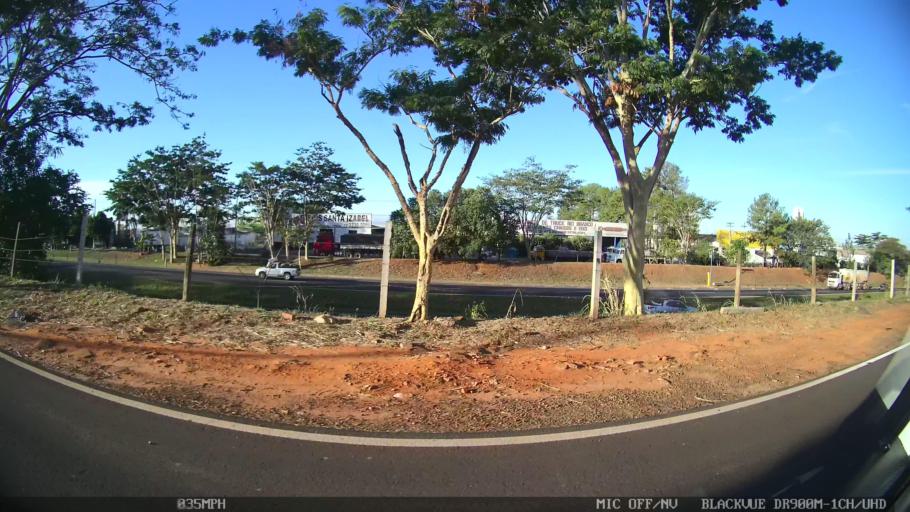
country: BR
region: Sao Paulo
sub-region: Sao Jose Do Rio Preto
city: Sao Jose do Rio Preto
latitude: -20.8561
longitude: -49.3397
